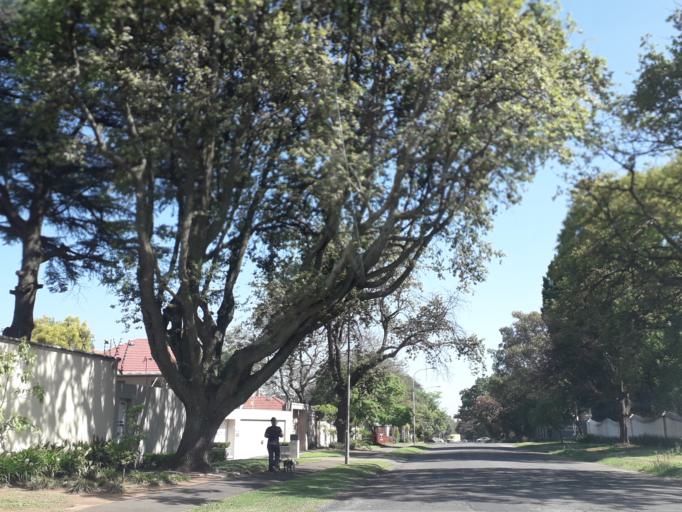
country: ZA
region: Gauteng
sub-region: City of Johannesburg Metropolitan Municipality
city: Johannesburg
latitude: -26.1606
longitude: 28.0618
